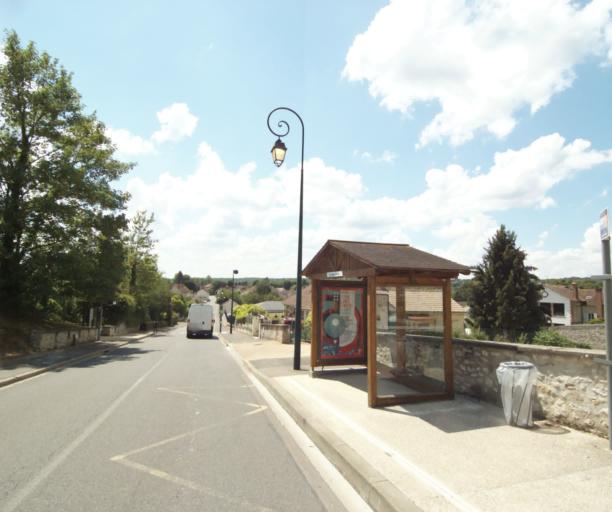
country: FR
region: Ile-de-France
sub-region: Departement de Seine-et-Marne
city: Hericy
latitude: 48.4487
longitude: 2.7664
